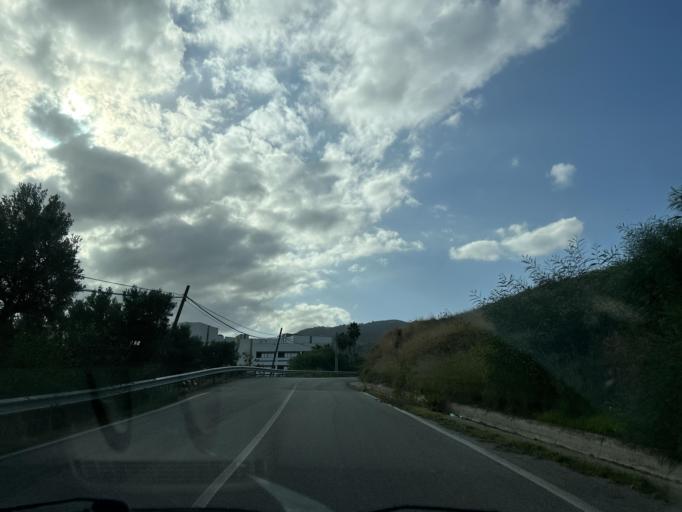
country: IT
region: Calabria
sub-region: Provincia di Catanzaro
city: Montepaone Lido
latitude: 38.7246
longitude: 16.5227
